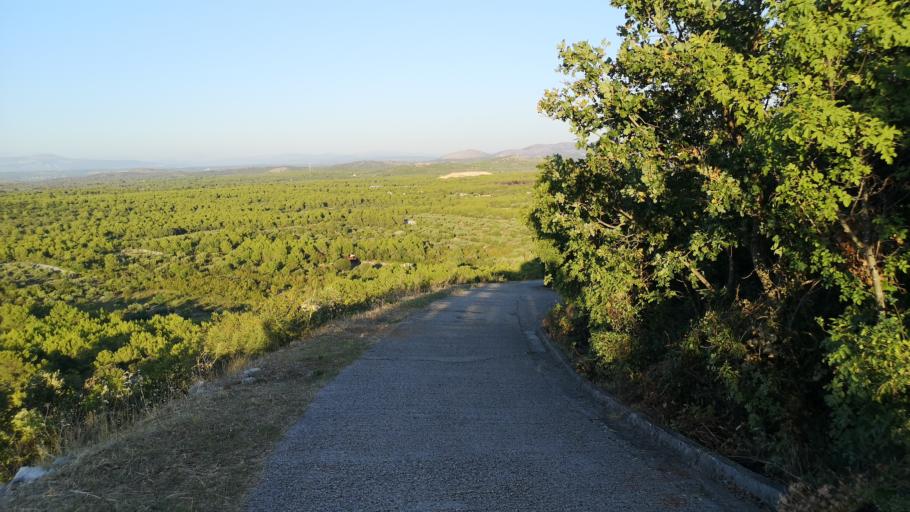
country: HR
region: Sibensko-Kniniska
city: Vodice
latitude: 43.7863
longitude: 15.7690
